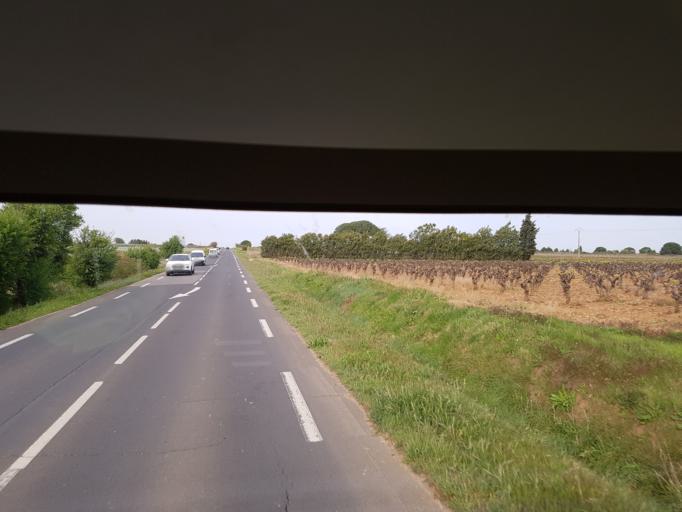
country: FR
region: Languedoc-Roussillon
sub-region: Departement de l'Herault
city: Marseillan
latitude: 43.3469
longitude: 3.5072
